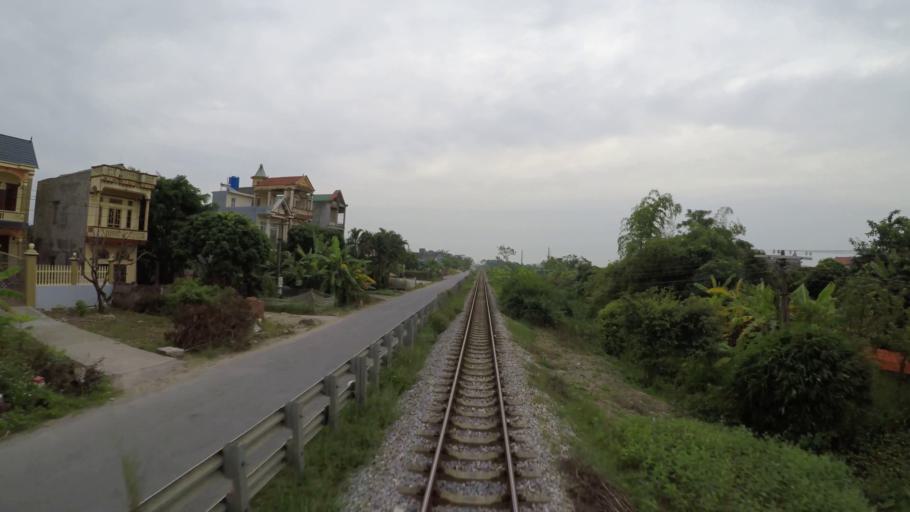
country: VN
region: Hung Yen
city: Ban Yen Nhan
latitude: 20.9655
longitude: 106.1110
